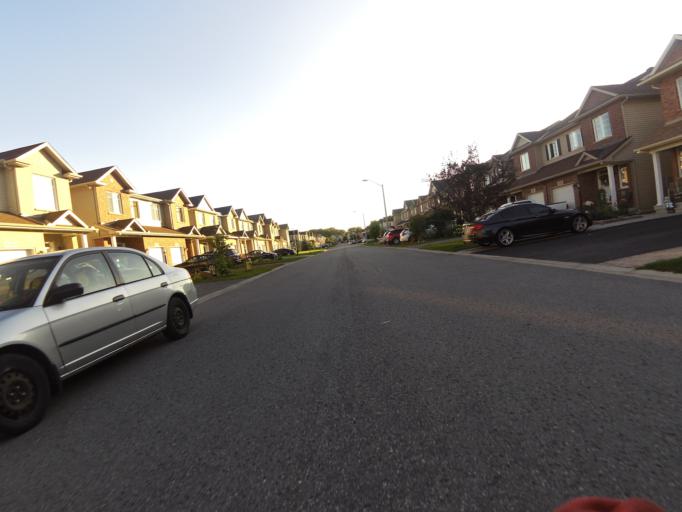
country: CA
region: Ontario
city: Bells Corners
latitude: 45.3614
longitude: -75.9291
